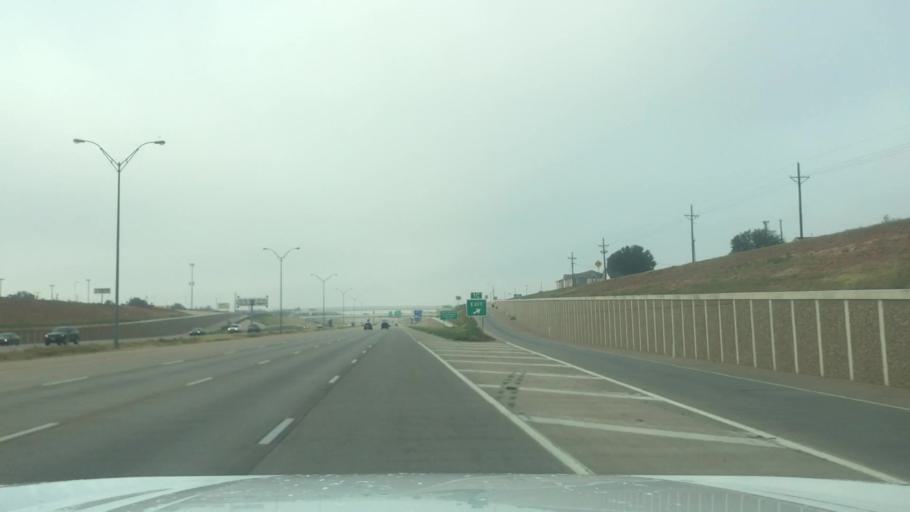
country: US
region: Texas
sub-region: Lubbock County
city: Lubbock
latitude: 33.5547
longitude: -101.8452
